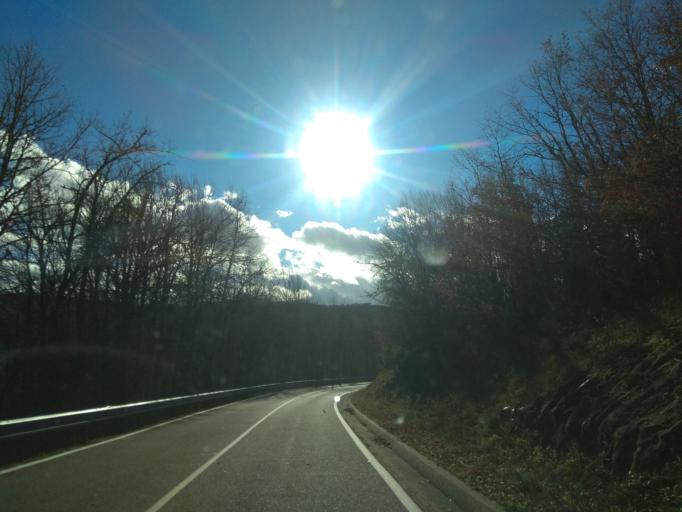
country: ES
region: Cantabria
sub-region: Provincia de Cantabria
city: San Martin de Elines
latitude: 42.9006
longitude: -3.8697
